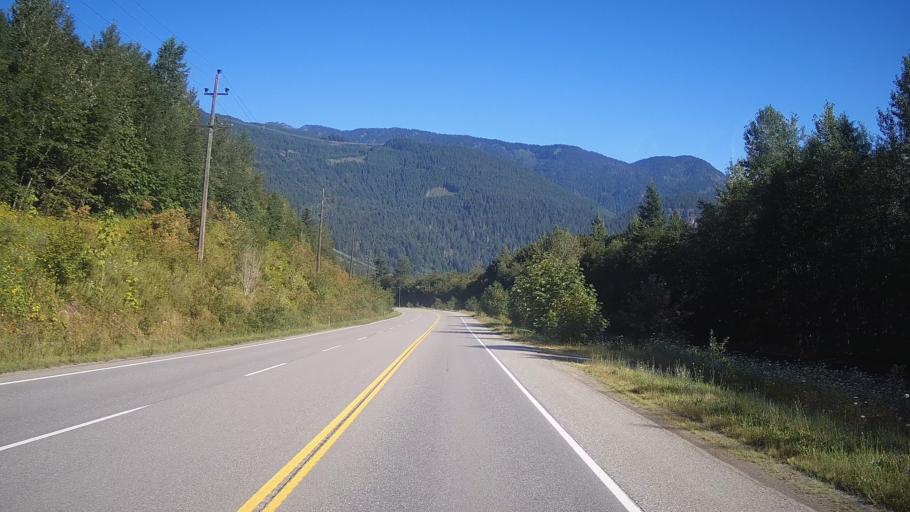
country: CA
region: British Columbia
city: Hope
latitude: 49.5359
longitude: -121.4294
